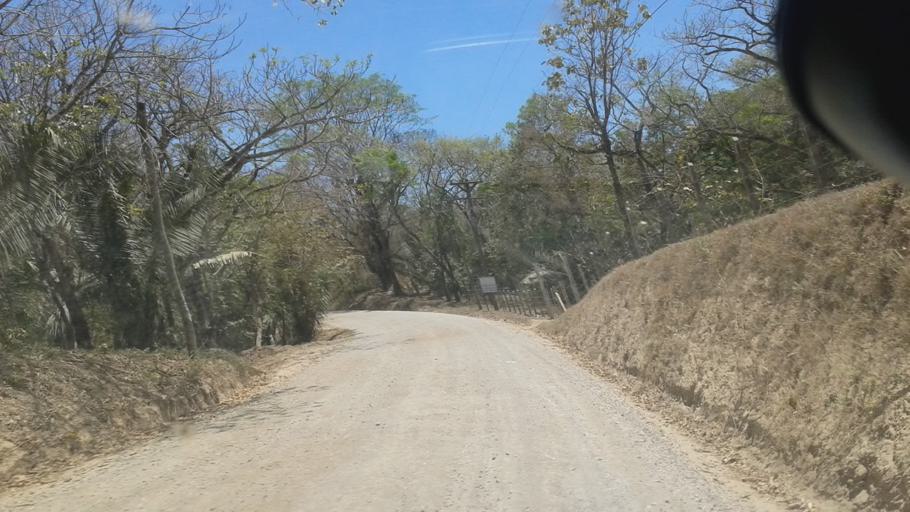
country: CR
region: Guanacaste
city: Samara
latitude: 10.0194
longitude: -85.7213
